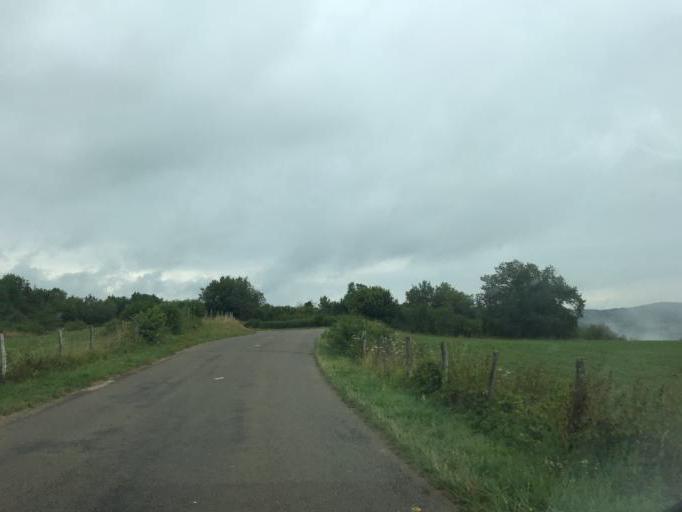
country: FR
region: Rhone-Alpes
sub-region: Departement de l'Ain
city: Arbent
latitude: 46.3150
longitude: 5.7437
